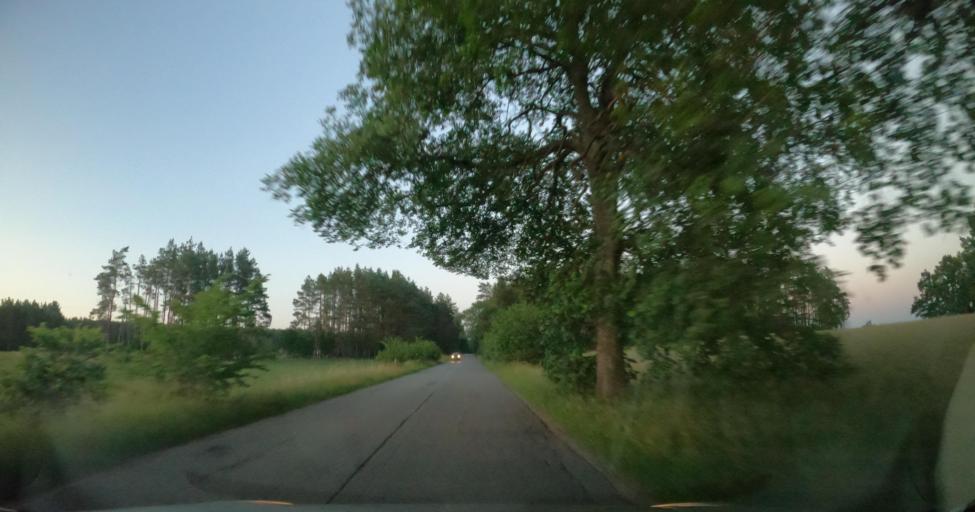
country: PL
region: Pomeranian Voivodeship
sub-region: Powiat wejherowski
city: Szemud
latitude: 54.4706
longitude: 18.1604
